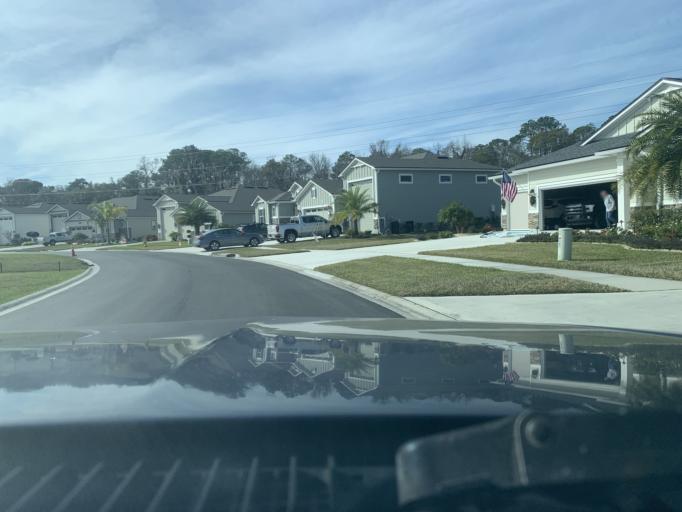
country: US
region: Florida
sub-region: Clay County
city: Green Cove Springs
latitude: 29.9792
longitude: -81.5296
